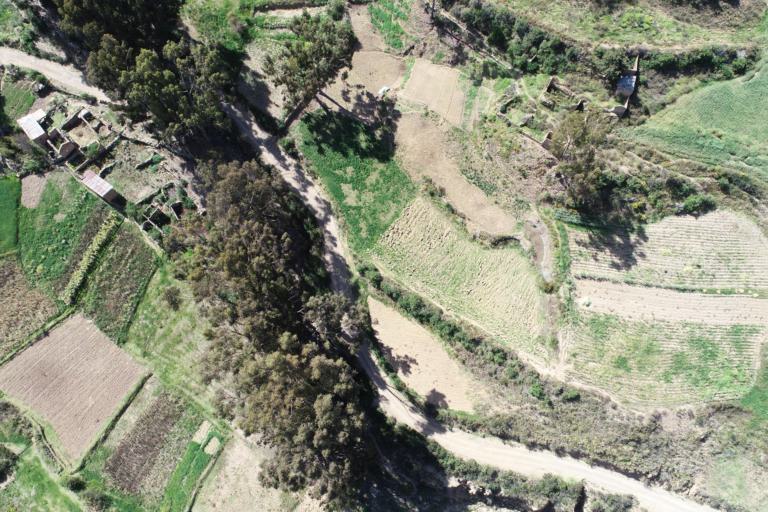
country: BO
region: La Paz
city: La Paz
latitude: -16.5547
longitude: -67.9868
